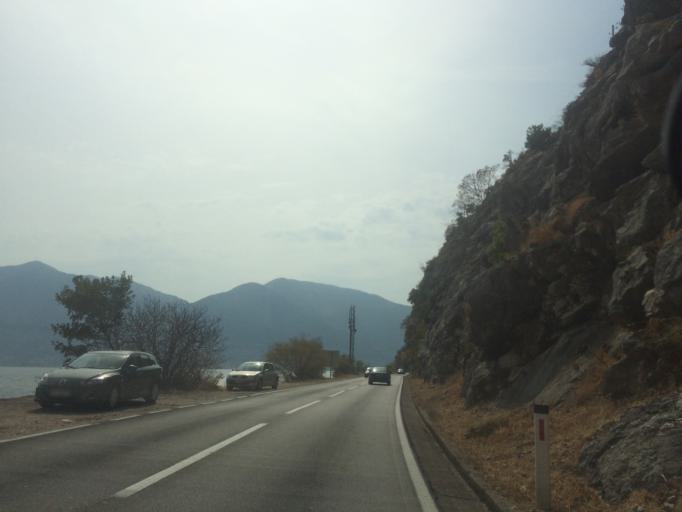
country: ME
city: Dobrota
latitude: 42.4897
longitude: 18.7527
